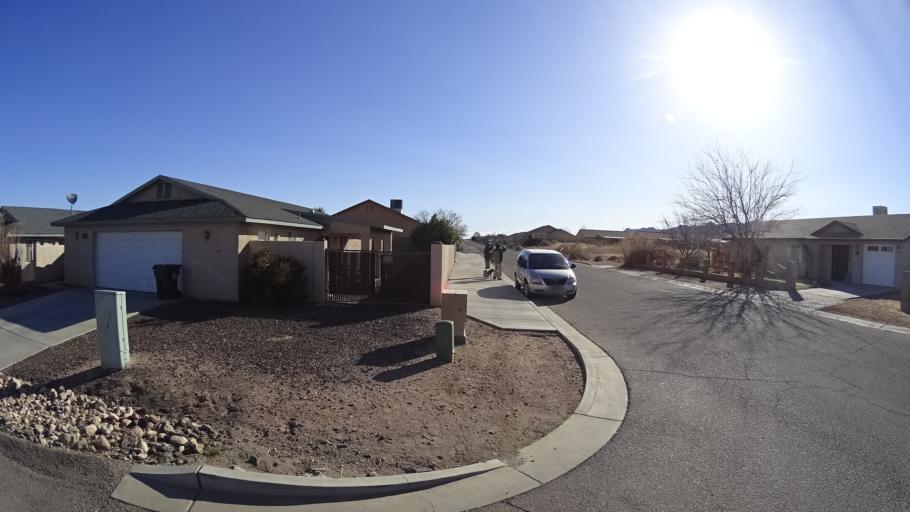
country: US
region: Arizona
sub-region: Mohave County
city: Kingman
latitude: 35.2122
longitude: -114.0093
